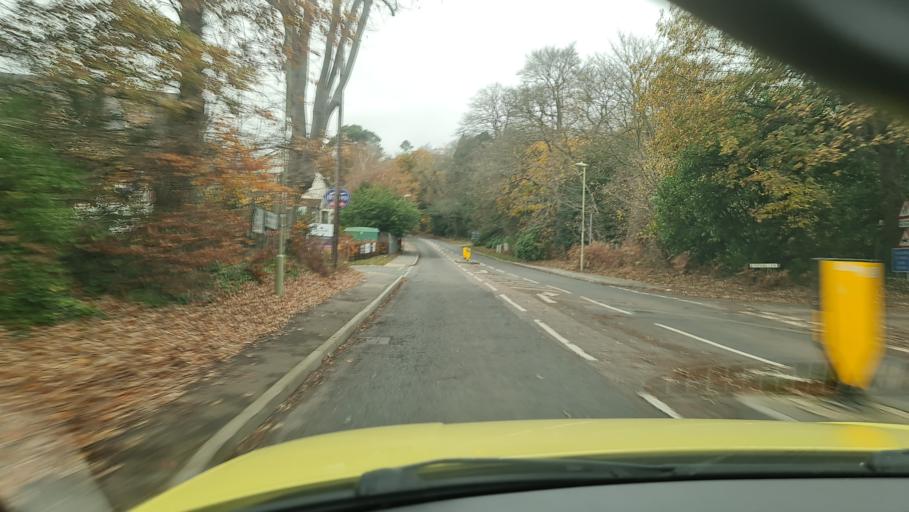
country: GB
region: England
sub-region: Hampshire
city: Farnborough
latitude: 51.3163
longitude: -0.7773
